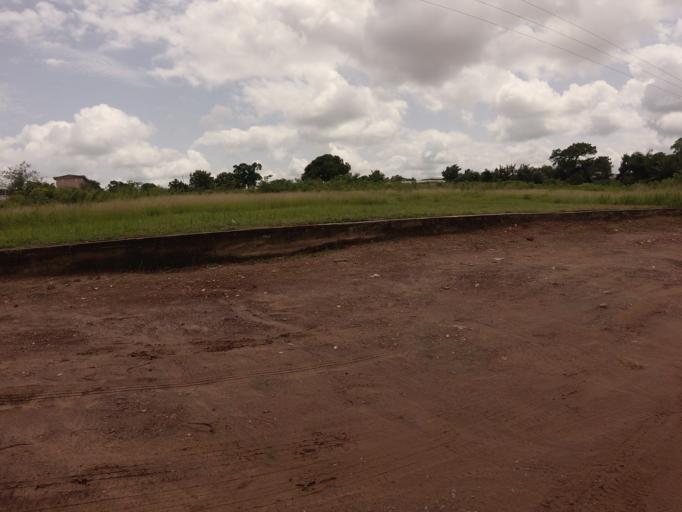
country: GH
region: Volta
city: Ho
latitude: 6.5981
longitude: 0.4854
